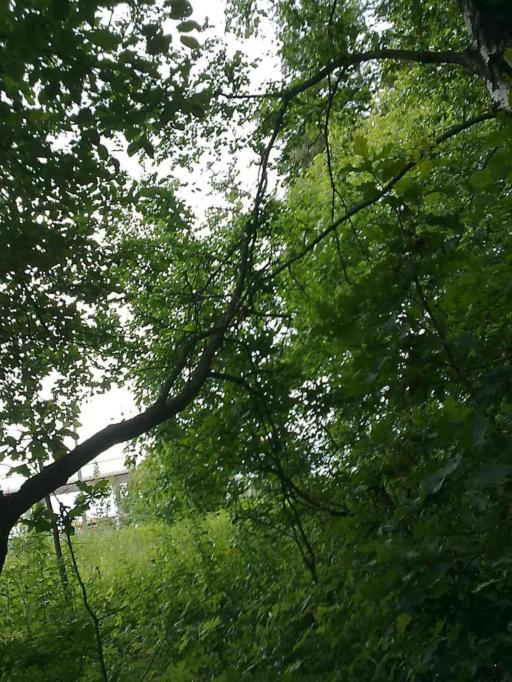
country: RU
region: Moskovskaya
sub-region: Leninskiy Rayon
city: Vnukovo
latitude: 55.6264
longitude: 37.2994
